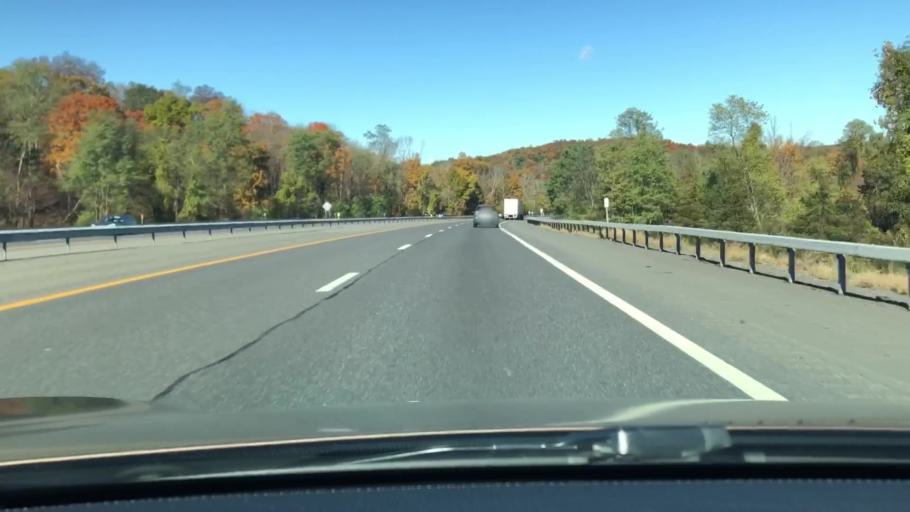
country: US
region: New York
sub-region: Ulster County
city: Rosendale Village
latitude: 41.8816
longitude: -74.0581
